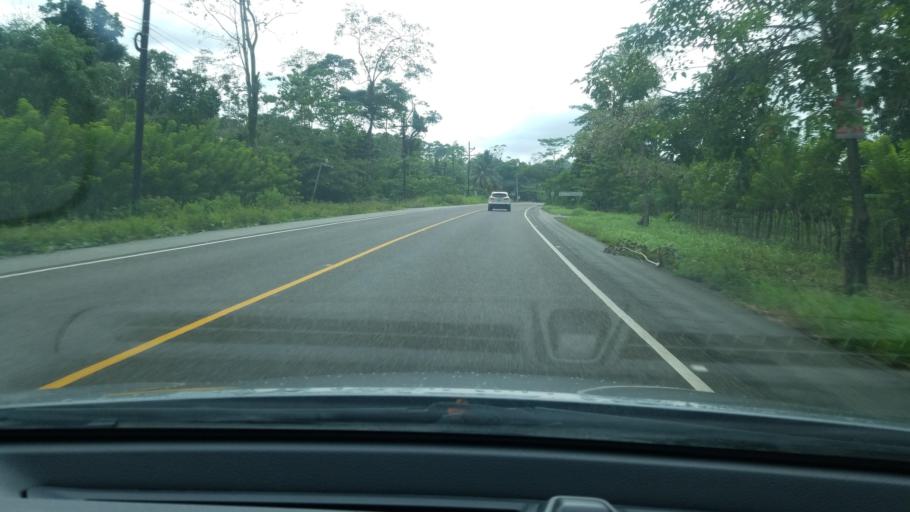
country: HN
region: Cortes
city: Potrerillos
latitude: 15.6118
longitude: -88.2831
